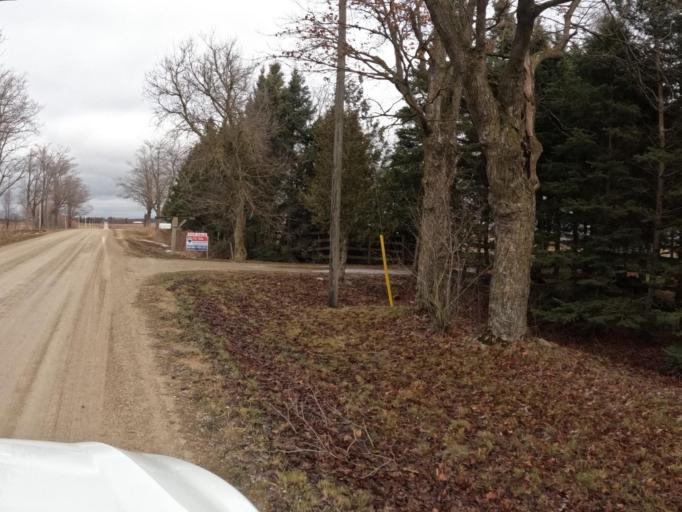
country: CA
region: Ontario
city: Shelburne
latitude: 43.9971
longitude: -80.4087
